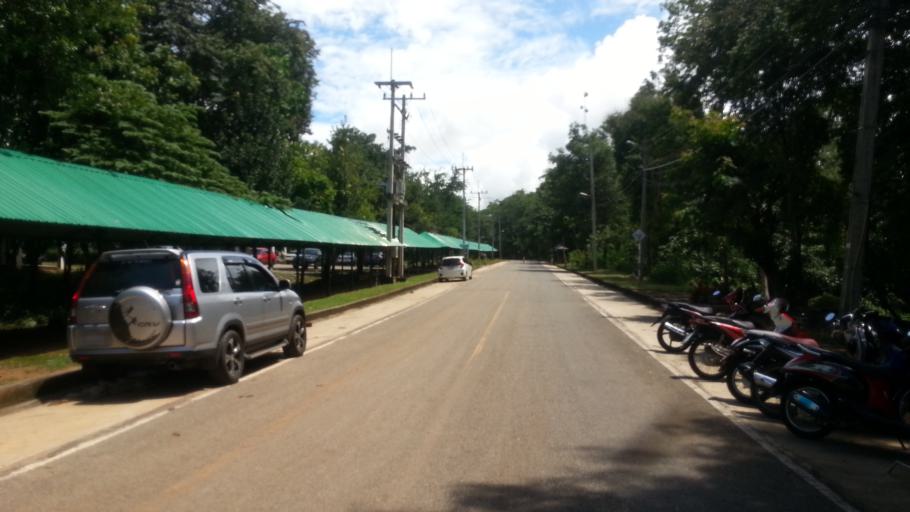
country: TH
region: Kanchanaburi
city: Sai Yok
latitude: 14.1237
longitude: 99.1540
